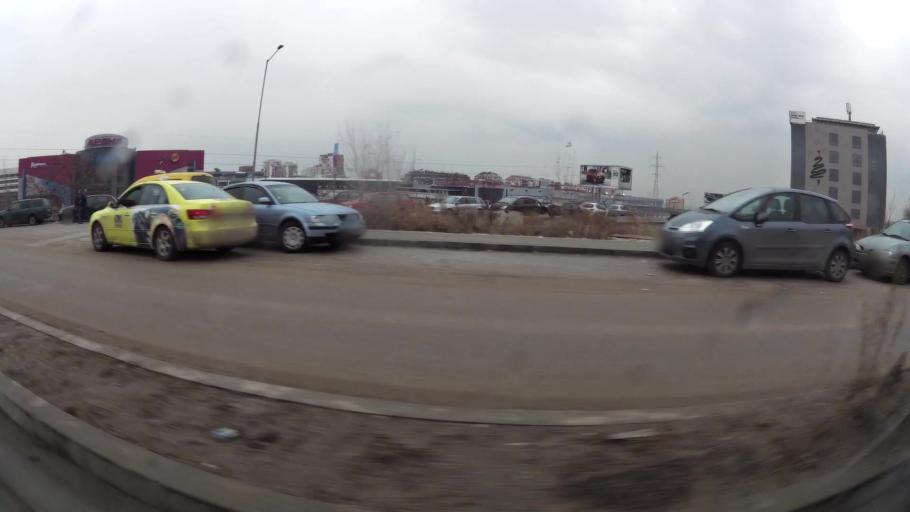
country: BG
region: Sofia-Capital
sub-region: Stolichna Obshtina
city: Sofia
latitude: 42.6227
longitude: 23.3765
